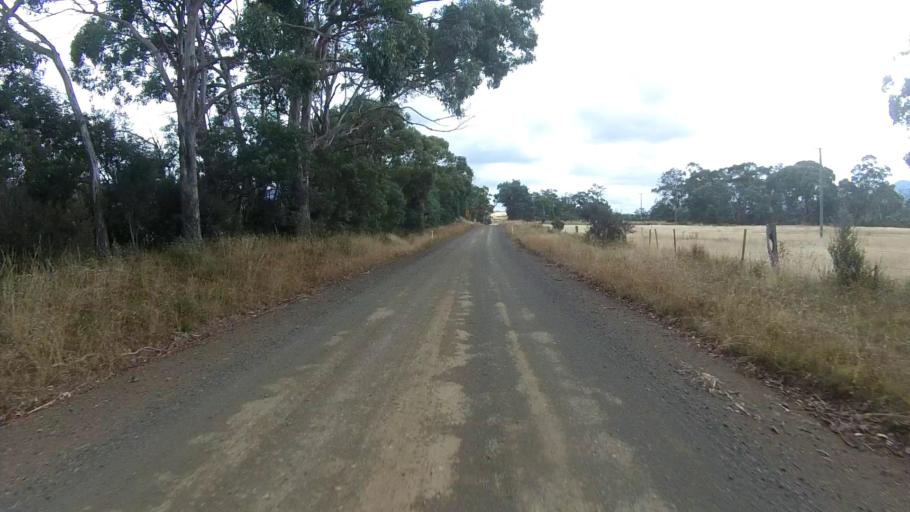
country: AU
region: Tasmania
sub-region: Break O'Day
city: St Helens
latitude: -41.8260
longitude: 147.9809
